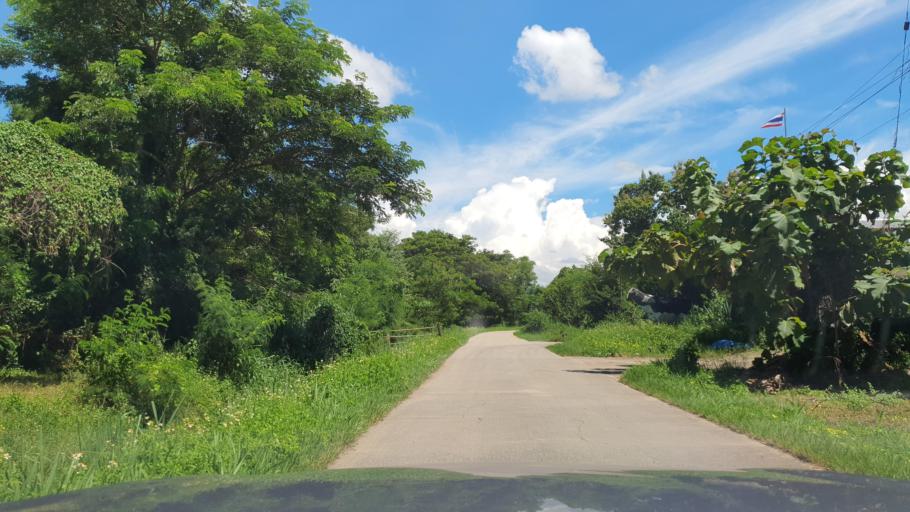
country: TH
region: Chiang Mai
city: San Kamphaeng
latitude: 18.7343
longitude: 99.1146
